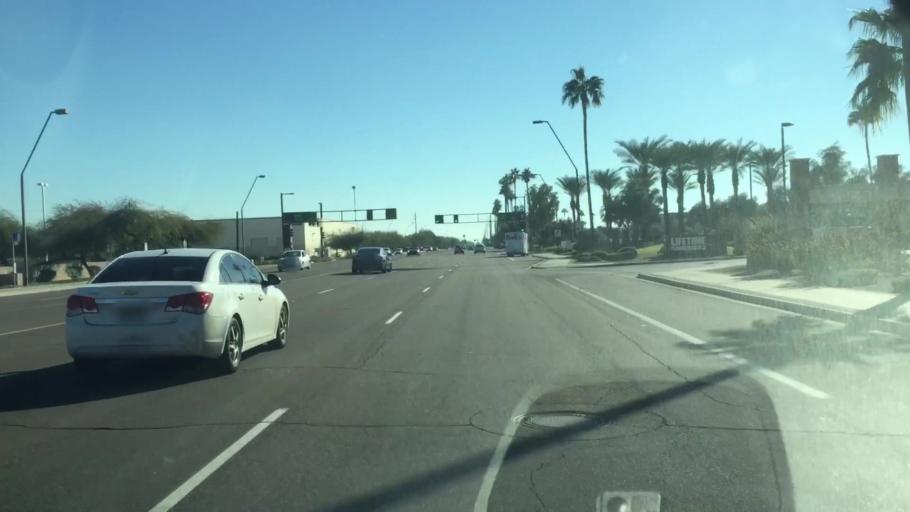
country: US
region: Arizona
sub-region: Maricopa County
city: Guadalupe
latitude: 33.3413
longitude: -111.9632
